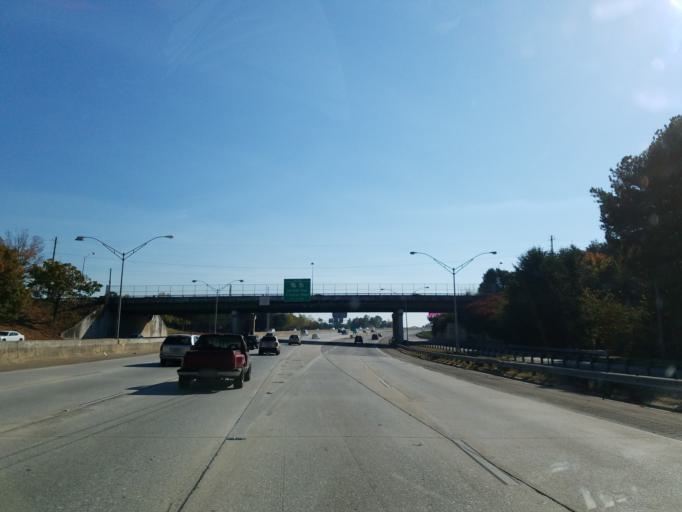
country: US
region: Georgia
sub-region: Fulton County
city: College Park
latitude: 33.6306
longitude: -84.4563
